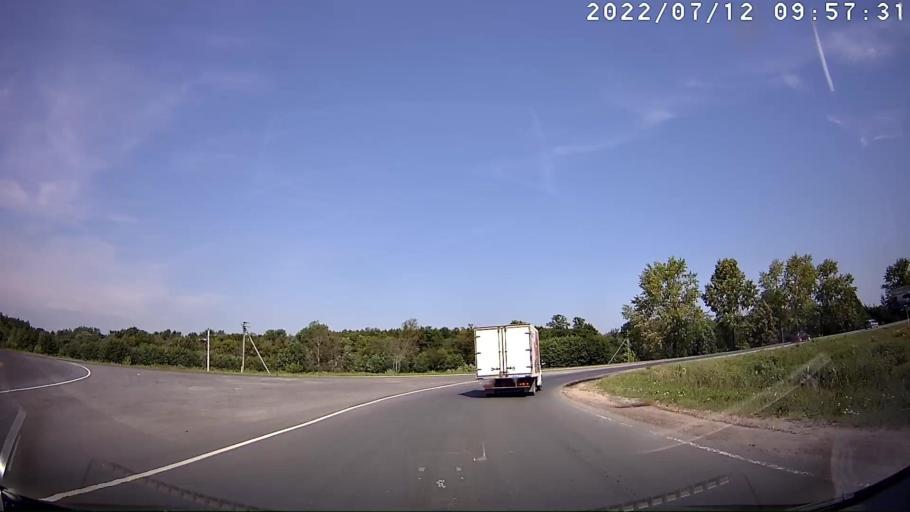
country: RU
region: Mariy-El
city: Yoshkar-Ola
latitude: 56.6451
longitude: 47.9400
